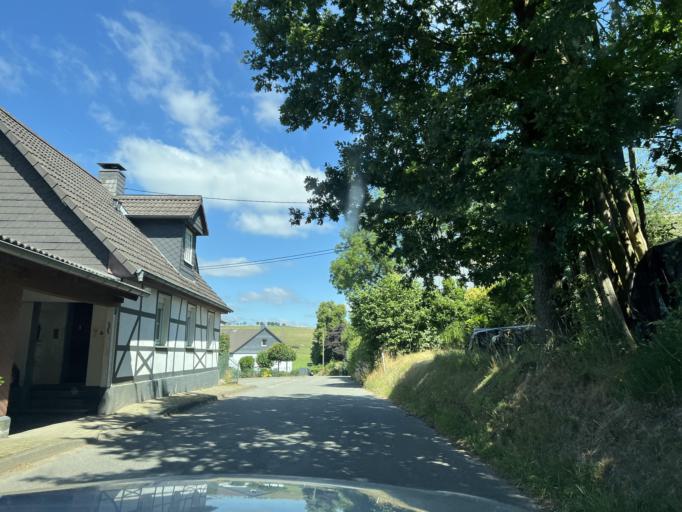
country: DE
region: North Rhine-Westphalia
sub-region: Regierungsbezirk Arnsberg
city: Drolshagen
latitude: 50.9850
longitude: 7.7375
